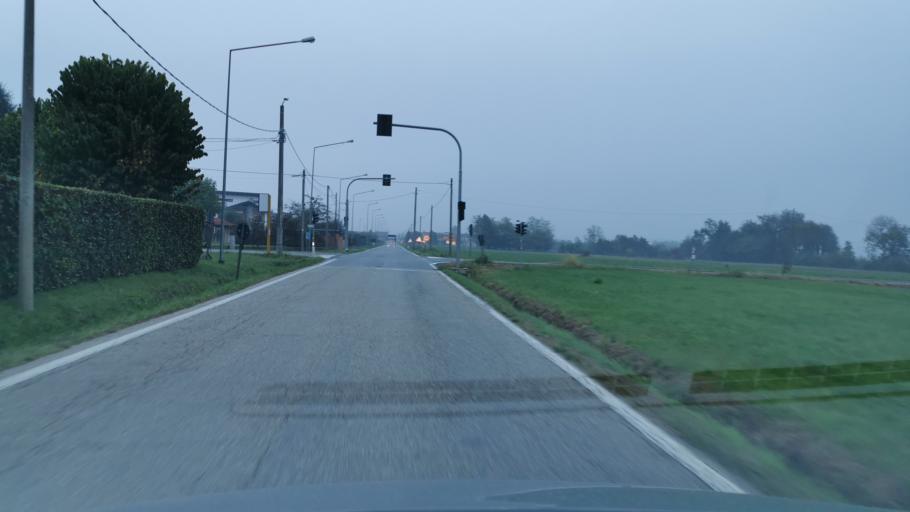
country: IT
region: Piedmont
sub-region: Provincia di Torino
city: Ciconio
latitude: 45.3299
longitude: 7.7620
